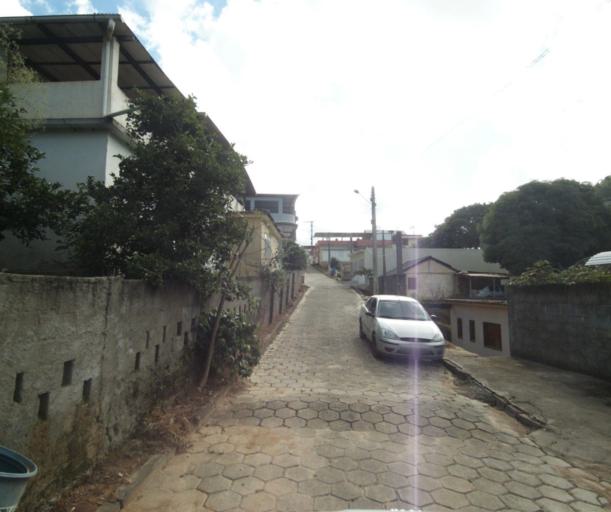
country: BR
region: Espirito Santo
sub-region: Irupi
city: Irupi
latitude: -20.5391
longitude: -41.6597
